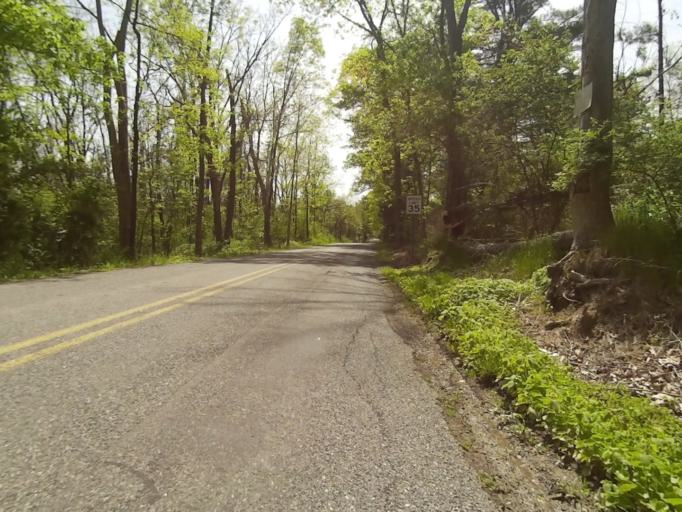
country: US
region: Pennsylvania
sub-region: Centre County
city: Houserville
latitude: 40.8746
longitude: -77.8766
